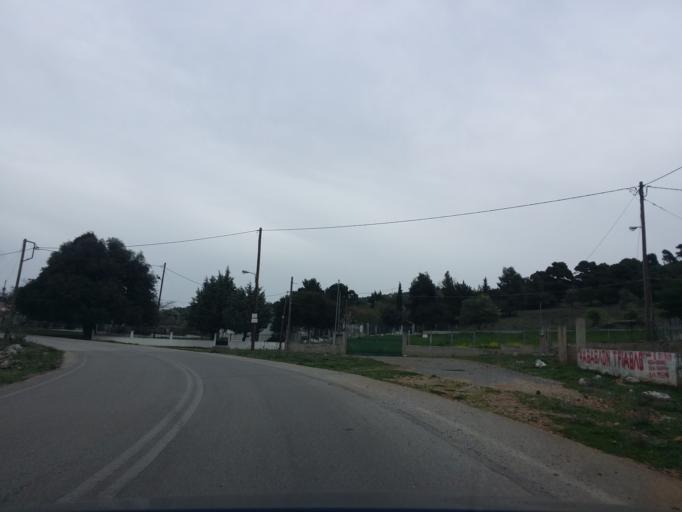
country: GR
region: Attica
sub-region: Nomarchia Dytikis Attikis
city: Vilia
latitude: 38.1439
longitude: 23.2945
